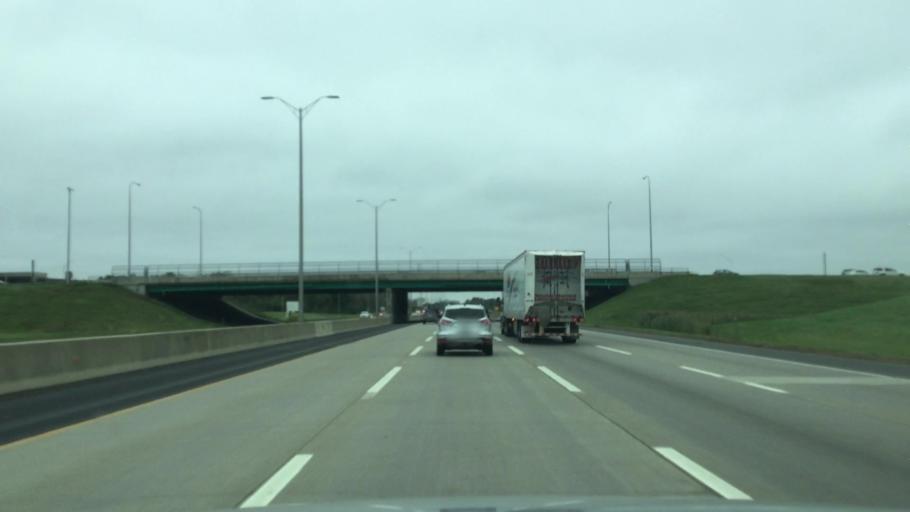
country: US
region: Illinois
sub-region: Lake County
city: Knollwood
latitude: 42.2414
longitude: -87.9016
